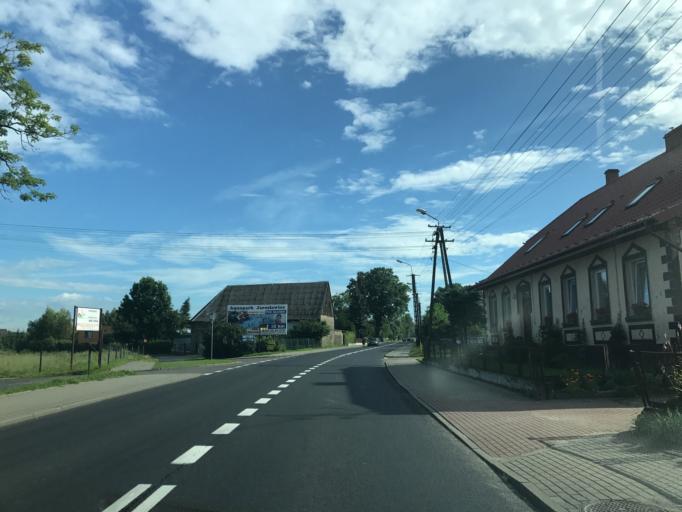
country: PL
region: West Pomeranian Voivodeship
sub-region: Powiat slawienski
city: Darlowo
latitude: 54.3102
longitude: 16.5186
